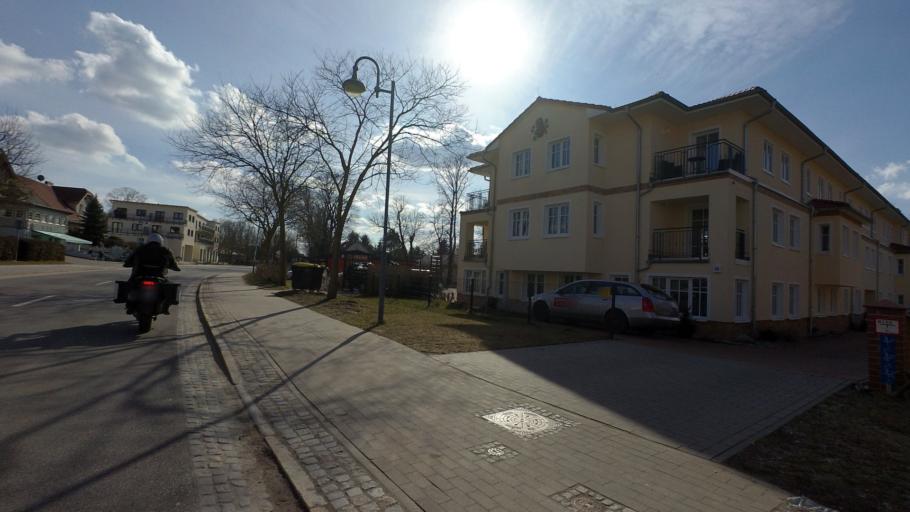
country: DE
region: Brandenburg
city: Wandlitz
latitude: 52.7526
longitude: 13.4716
